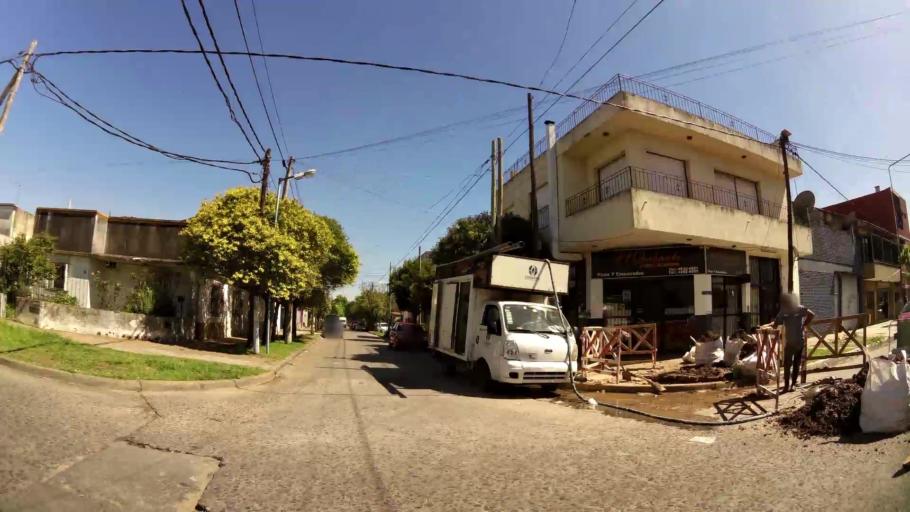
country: AR
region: Buenos Aires
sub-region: Partido de Quilmes
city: Quilmes
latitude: -34.7189
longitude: -58.2947
